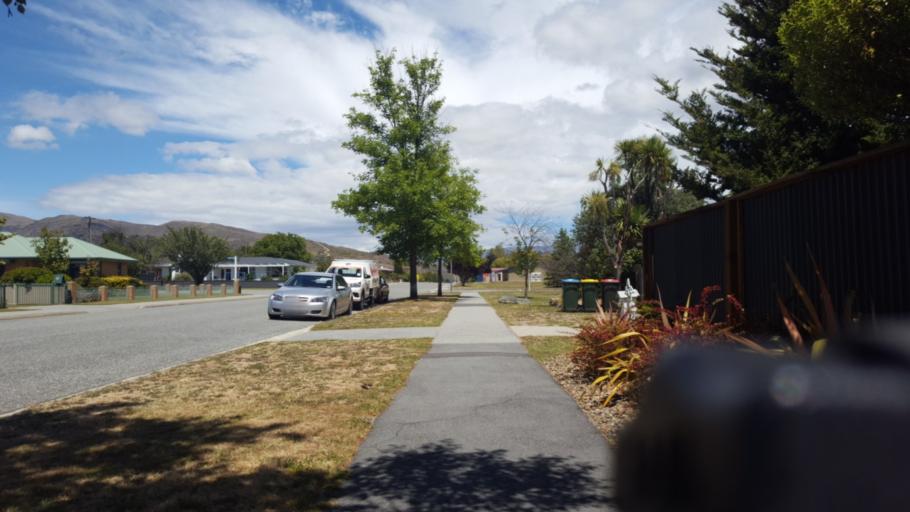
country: NZ
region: Otago
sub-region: Queenstown-Lakes District
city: Wanaka
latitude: -45.0429
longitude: 169.2053
